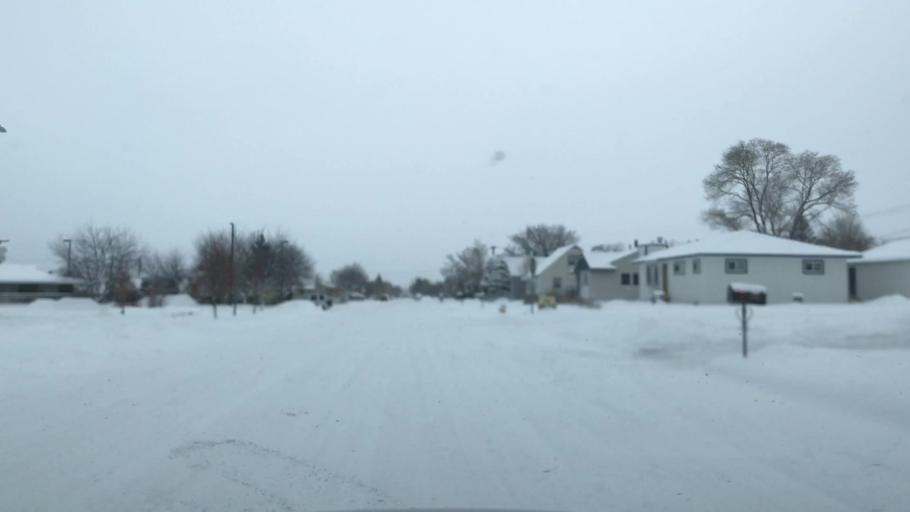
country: US
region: Montana
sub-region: Lewis and Clark County
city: Helena
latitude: 46.5932
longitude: -112.0114
